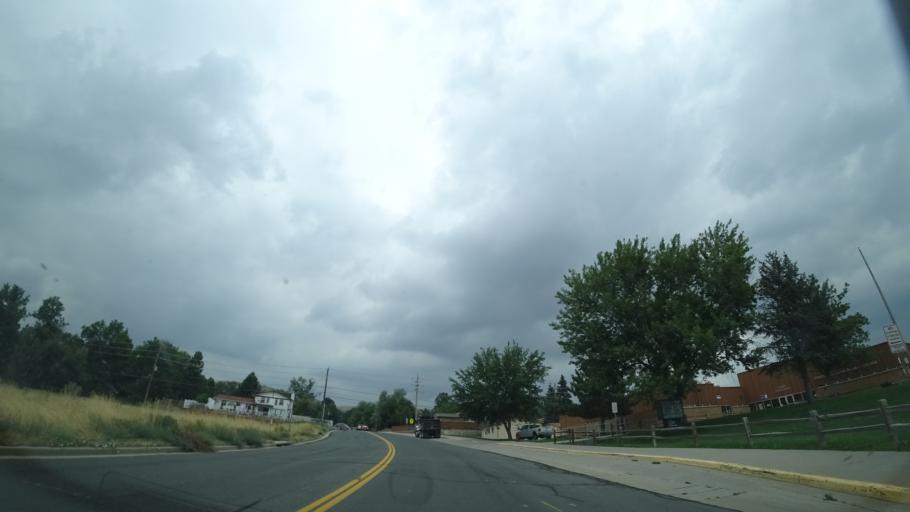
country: US
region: Colorado
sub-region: Jefferson County
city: West Pleasant View
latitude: 39.7023
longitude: -105.1462
